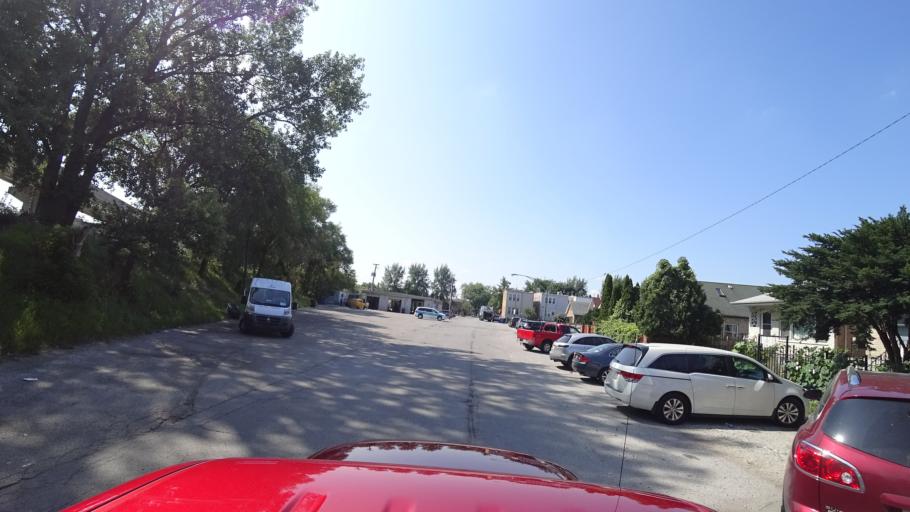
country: US
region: Illinois
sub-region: Cook County
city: Chicago
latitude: 41.8241
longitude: -87.6862
